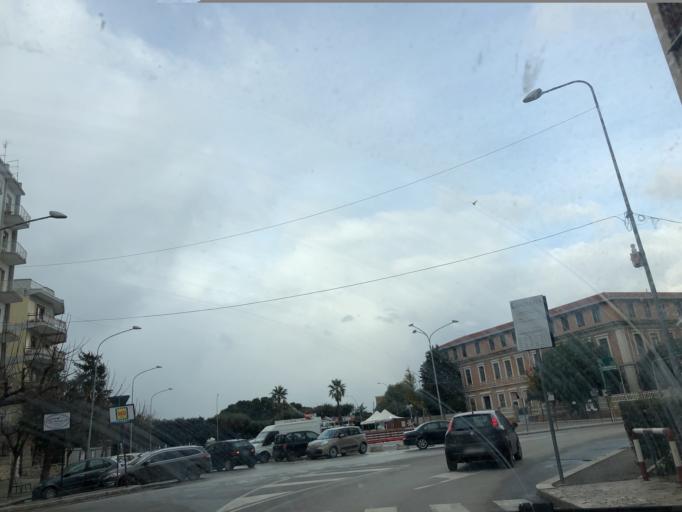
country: IT
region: Apulia
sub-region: Provincia di Foggia
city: Lucera
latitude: 41.5096
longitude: 15.3308
